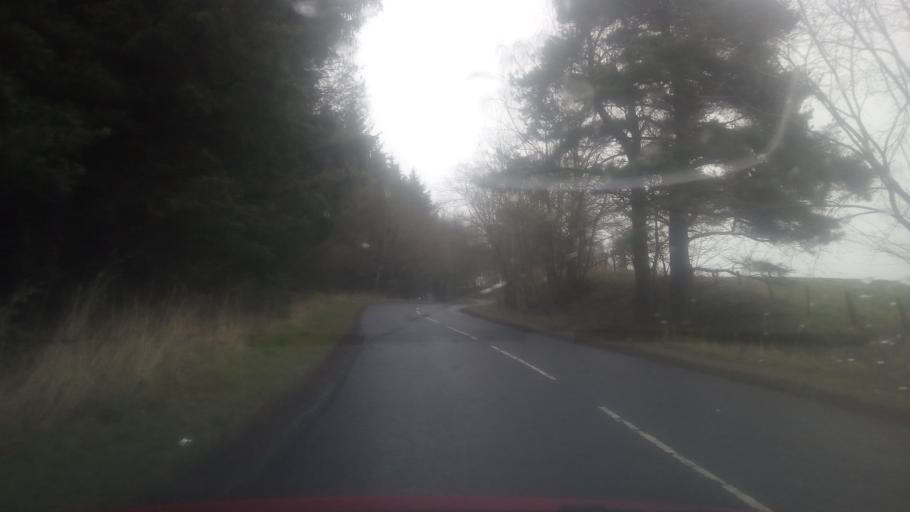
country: GB
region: Scotland
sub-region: The Scottish Borders
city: Earlston
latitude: 55.6771
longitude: -2.5726
